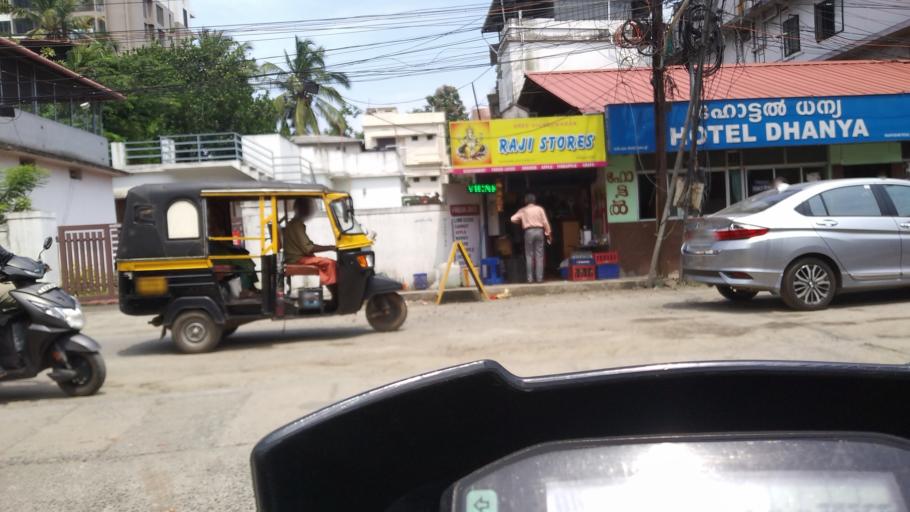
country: IN
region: Kerala
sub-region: Ernakulam
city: Cochin
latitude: 9.9615
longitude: 76.2897
